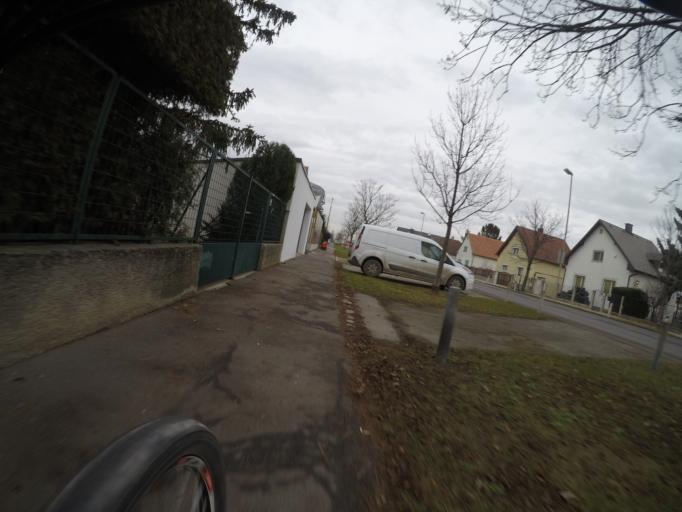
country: AT
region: Lower Austria
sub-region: Politischer Bezirk Modling
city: Vosendorf
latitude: 48.1332
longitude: 16.3260
